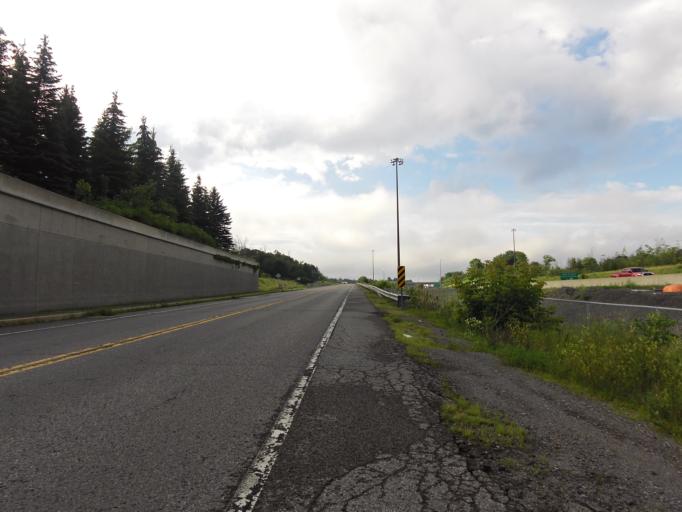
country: CA
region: Ontario
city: Bells Corners
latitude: 45.3306
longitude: -75.8083
